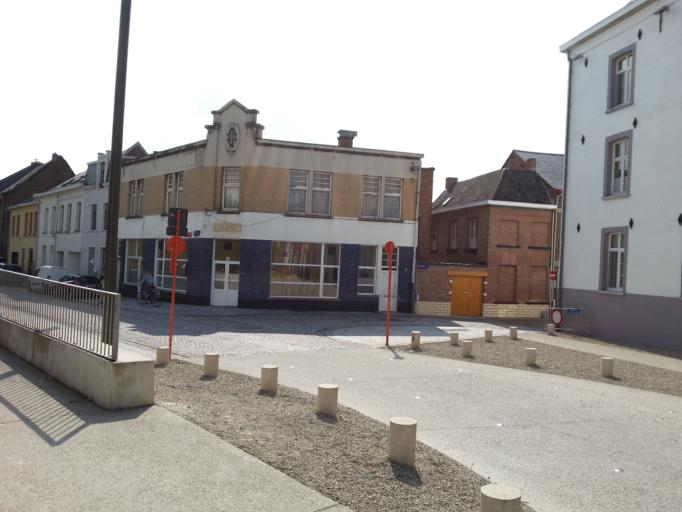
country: BE
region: Flanders
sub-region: Provincie Antwerpen
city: Mechelen
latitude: 51.0341
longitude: 4.4787
